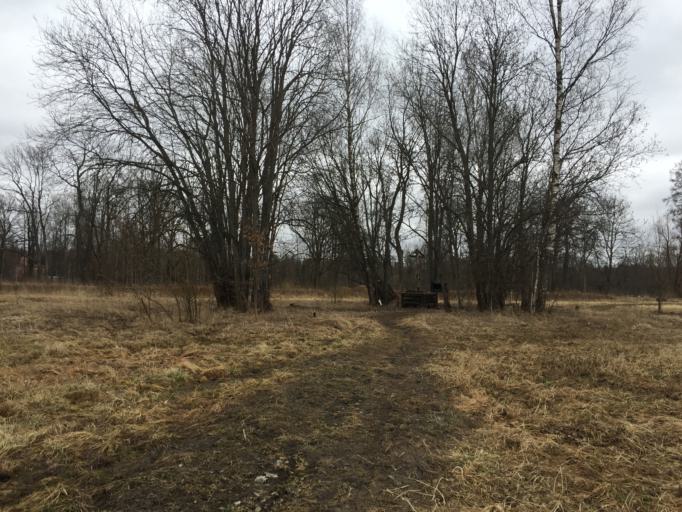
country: RU
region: St.-Petersburg
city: Pushkin
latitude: 59.7252
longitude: 30.3700
